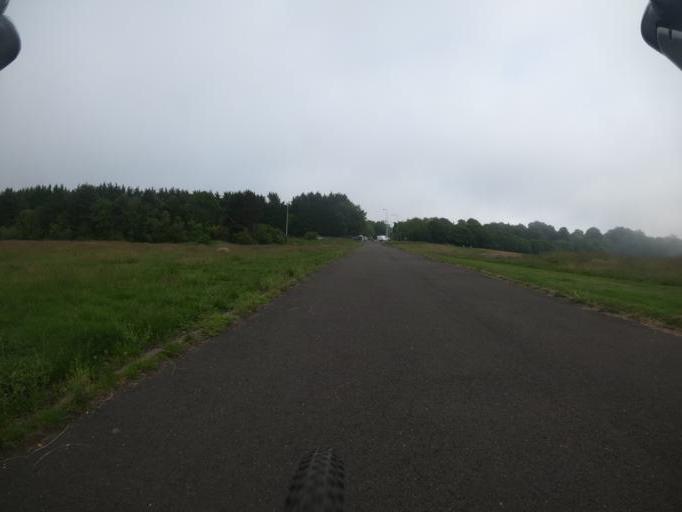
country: GB
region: Scotland
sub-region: Edinburgh
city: Edinburgh
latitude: 55.9824
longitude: -3.2526
